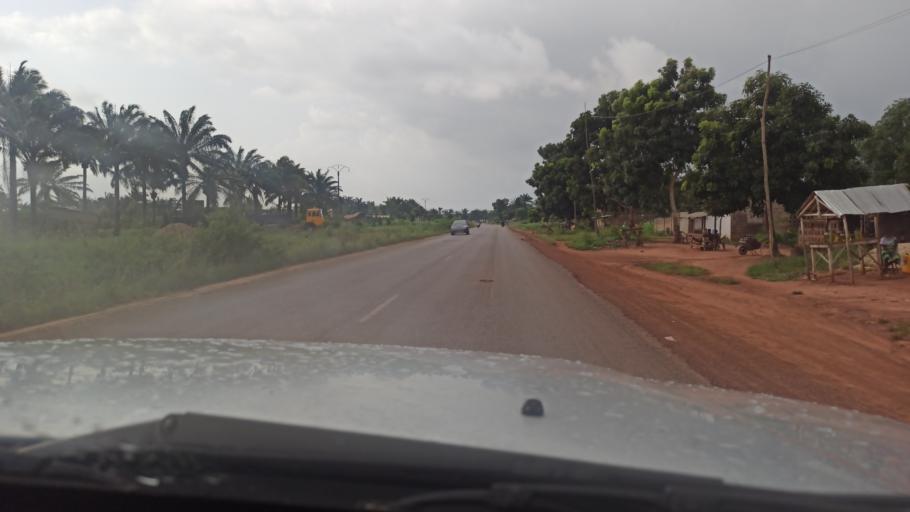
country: BJ
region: Queme
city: Porto-Novo
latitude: 6.5676
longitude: 2.5791
